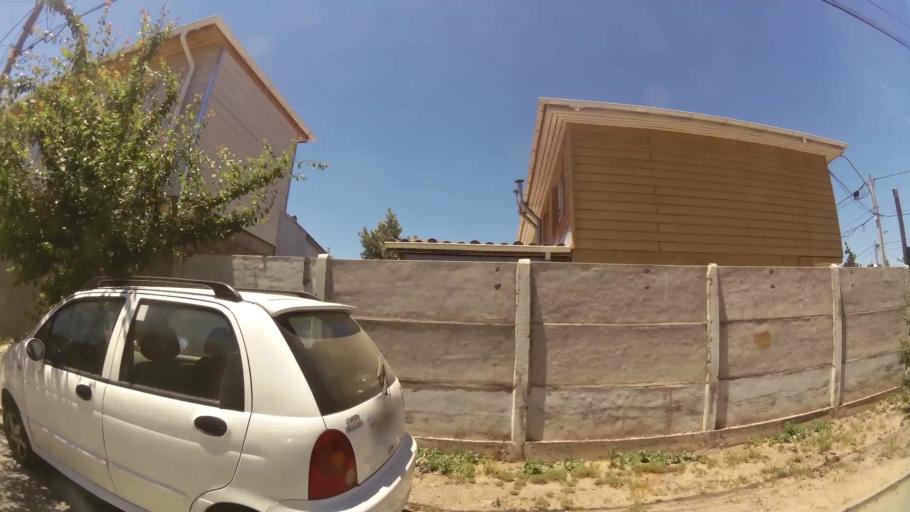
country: CL
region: Santiago Metropolitan
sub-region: Provincia de Maipo
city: San Bernardo
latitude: -33.6058
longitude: -70.6715
